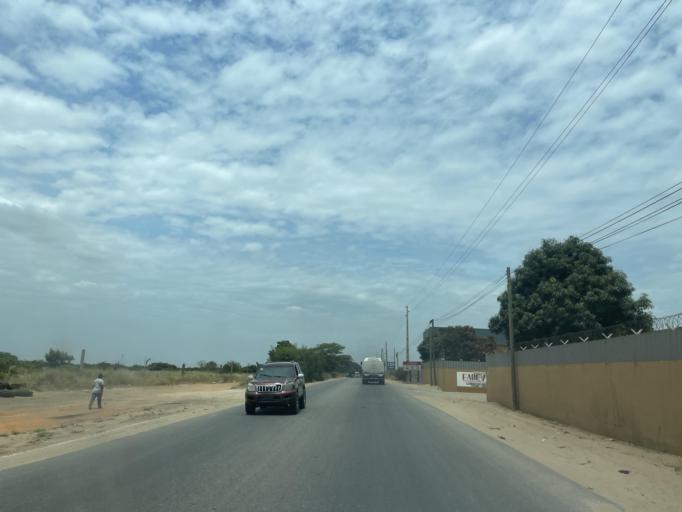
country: AO
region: Luanda
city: Luanda
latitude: -8.9396
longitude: 13.3883
